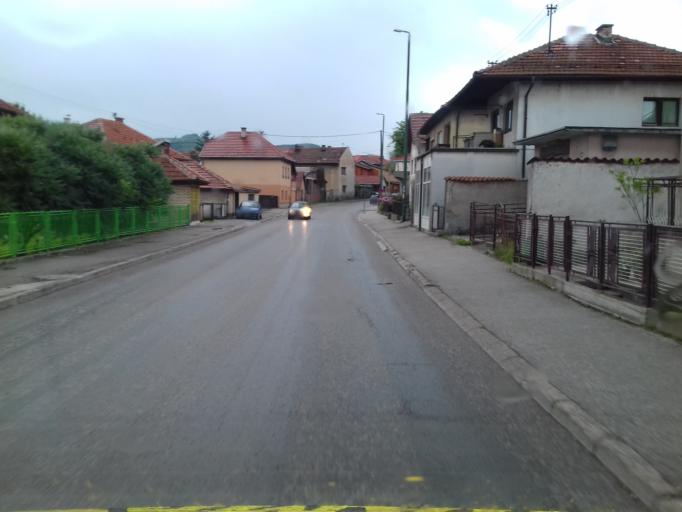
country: BA
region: Federation of Bosnia and Herzegovina
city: Visoko
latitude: 43.9895
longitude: 18.1758
